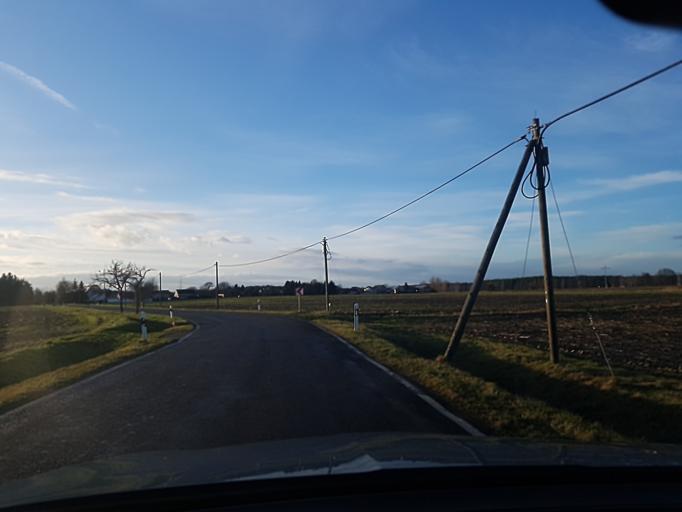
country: DE
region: Brandenburg
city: Schilda
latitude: 51.5883
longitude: 13.3920
